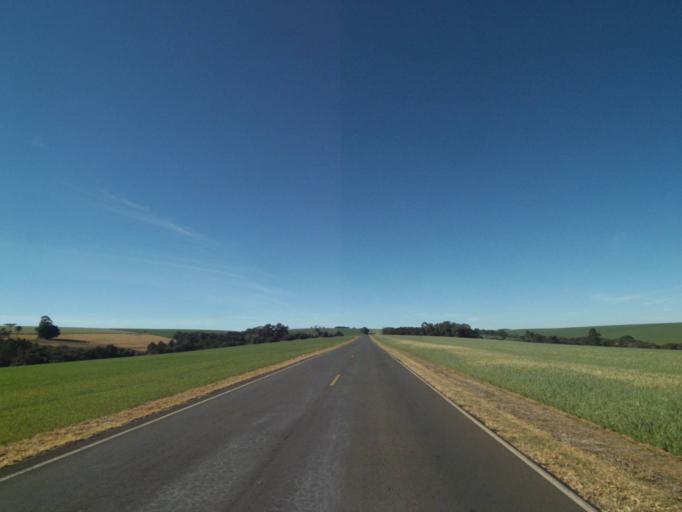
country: BR
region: Parana
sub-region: Tibagi
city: Tibagi
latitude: -24.5299
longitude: -50.3200
